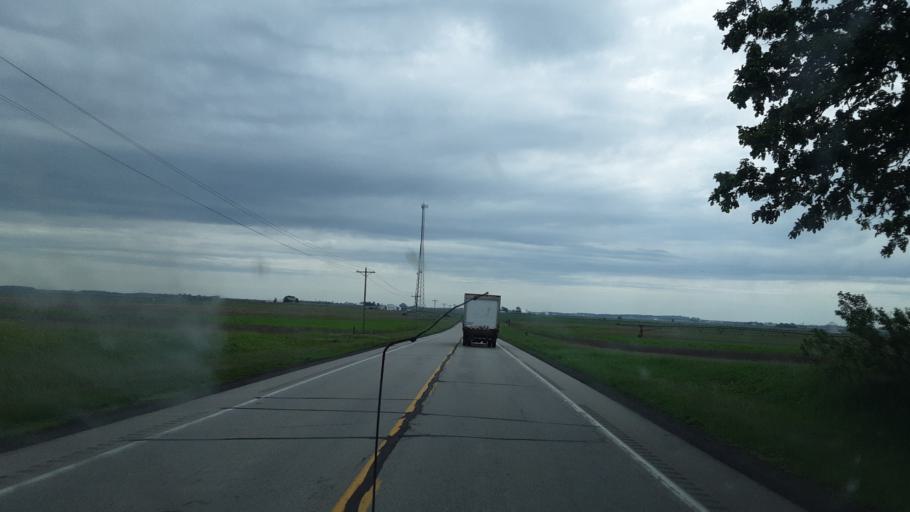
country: US
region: Illinois
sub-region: Mason County
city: Manito
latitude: 40.3036
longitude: -89.7781
